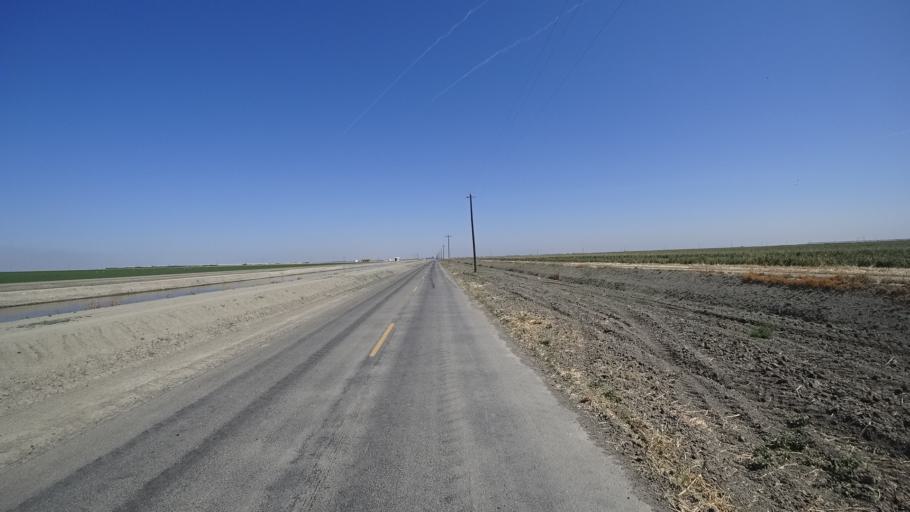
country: US
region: California
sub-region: Tulare County
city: Alpaugh
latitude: 35.9862
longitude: -119.5362
